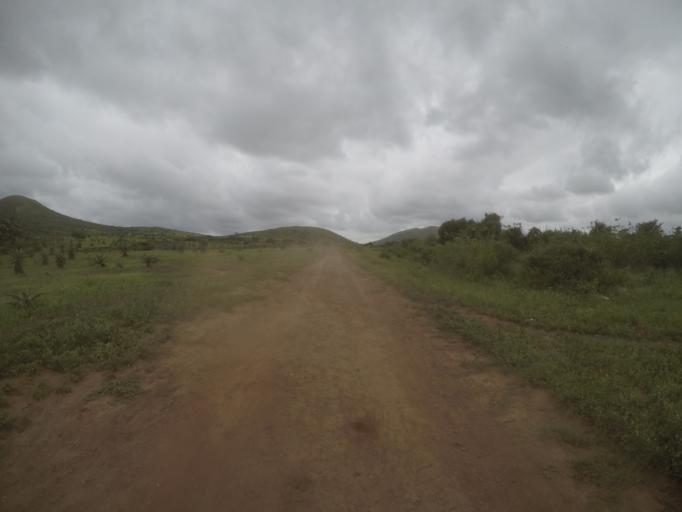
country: ZA
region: KwaZulu-Natal
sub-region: uThungulu District Municipality
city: Empangeni
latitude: -28.6084
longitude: 31.8650
